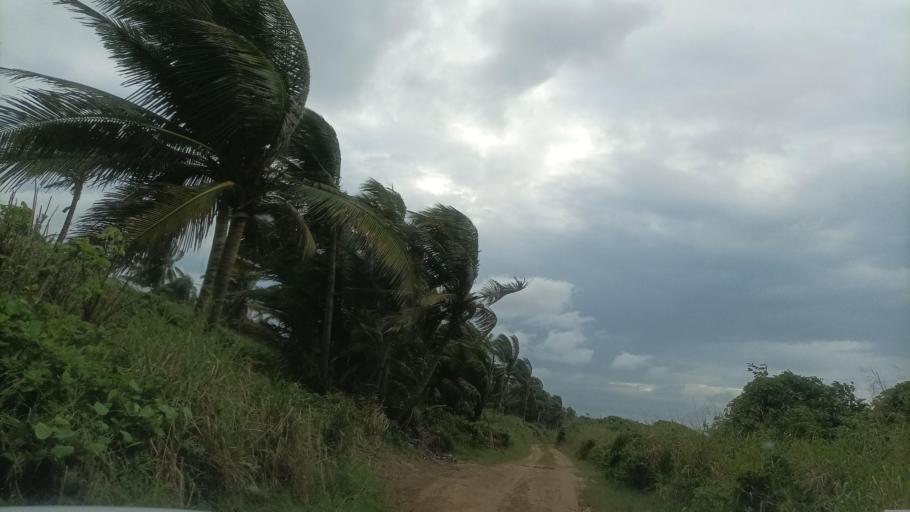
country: MX
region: Veracruz
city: Agua Dulce
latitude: 18.1823
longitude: -94.2622
